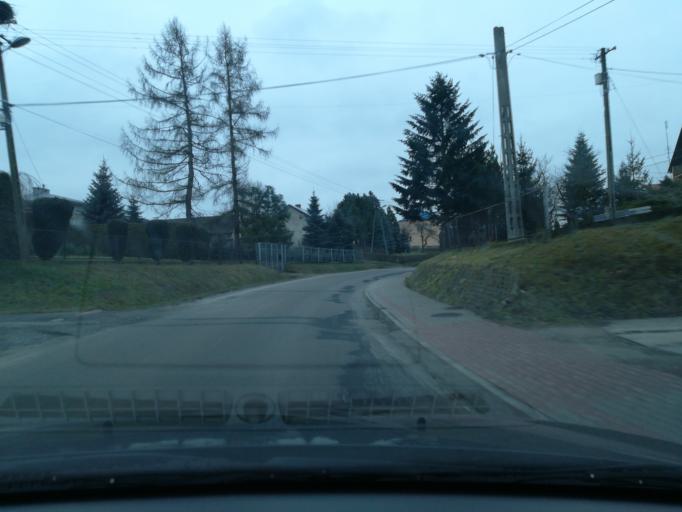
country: PL
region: Subcarpathian Voivodeship
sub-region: Powiat lancucki
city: Kosina
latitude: 50.0814
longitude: 22.3257
